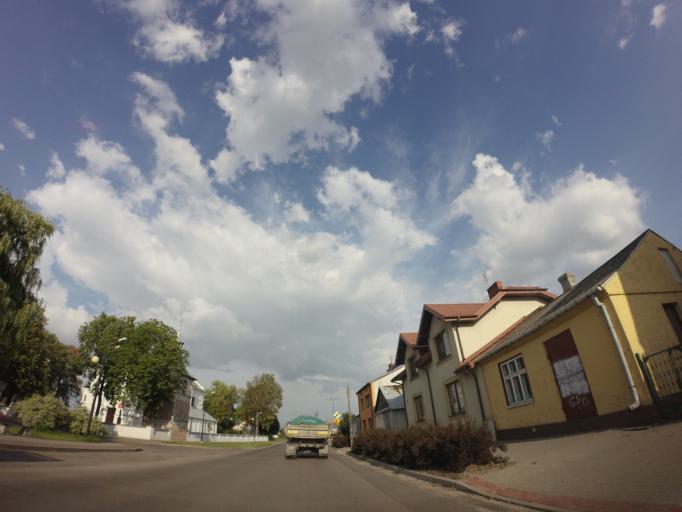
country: PL
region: Lublin Voivodeship
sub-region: Powiat lukowski
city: Adamow
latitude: 51.7433
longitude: 22.2629
